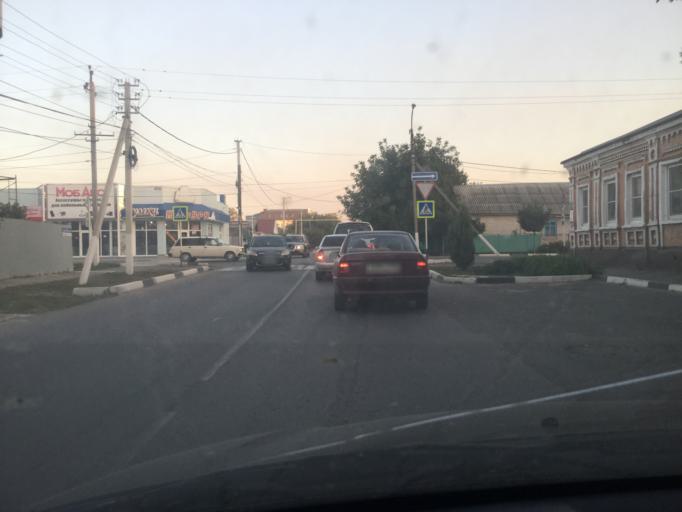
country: RU
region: Krasnodarskiy
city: Slavyansk-na-Kubani
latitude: 45.2562
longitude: 38.1224
